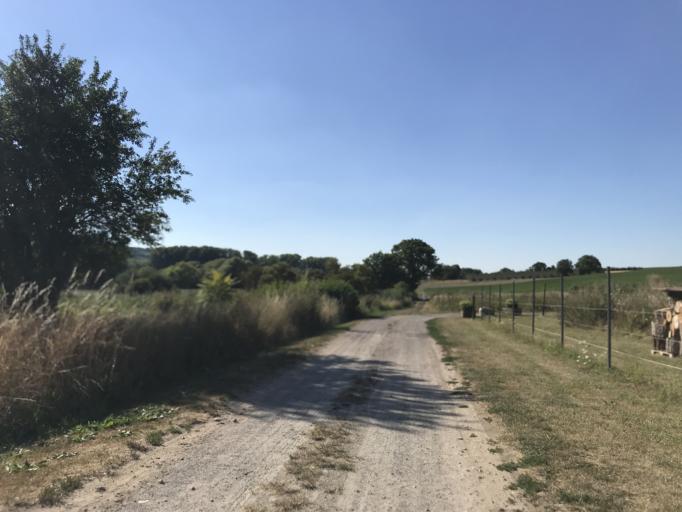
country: DE
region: Rheinland-Pfalz
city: Schwabenheim
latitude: 49.9329
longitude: 8.0896
